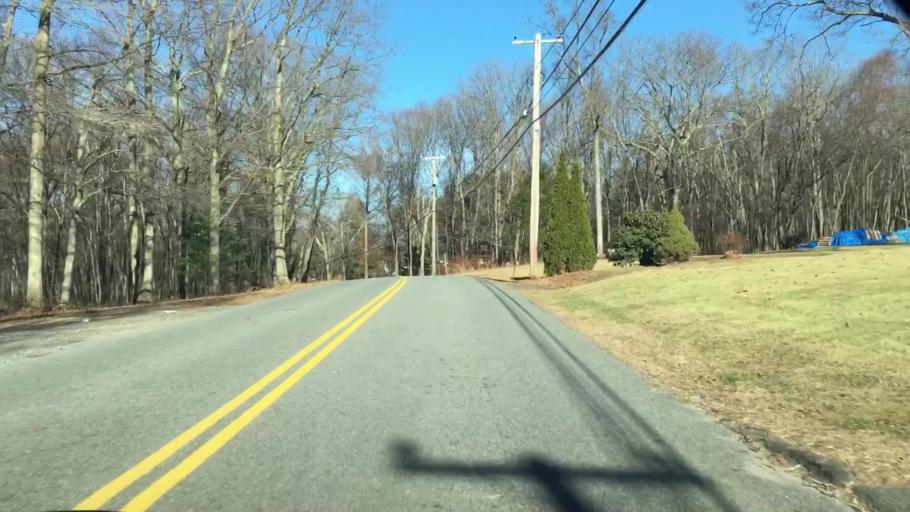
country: US
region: Connecticut
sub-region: Tolland County
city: Tolland
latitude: 41.8868
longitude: -72.3866
